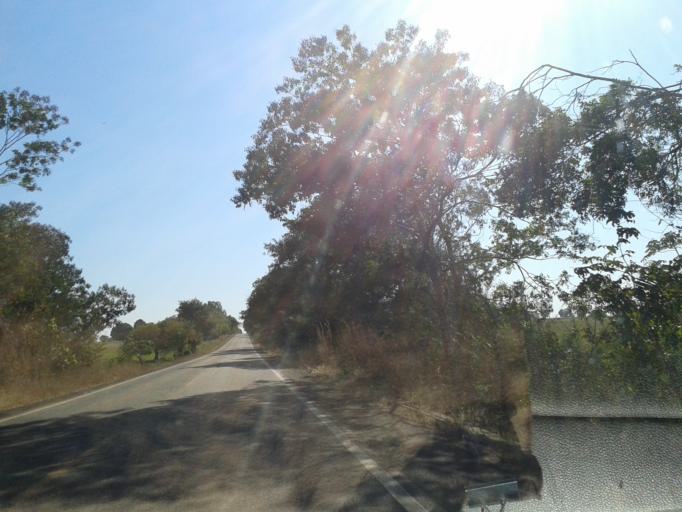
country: BR
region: Goias
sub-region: Mozarlandia
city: Mozarlandia
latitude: -14.6080
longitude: -50.5141
